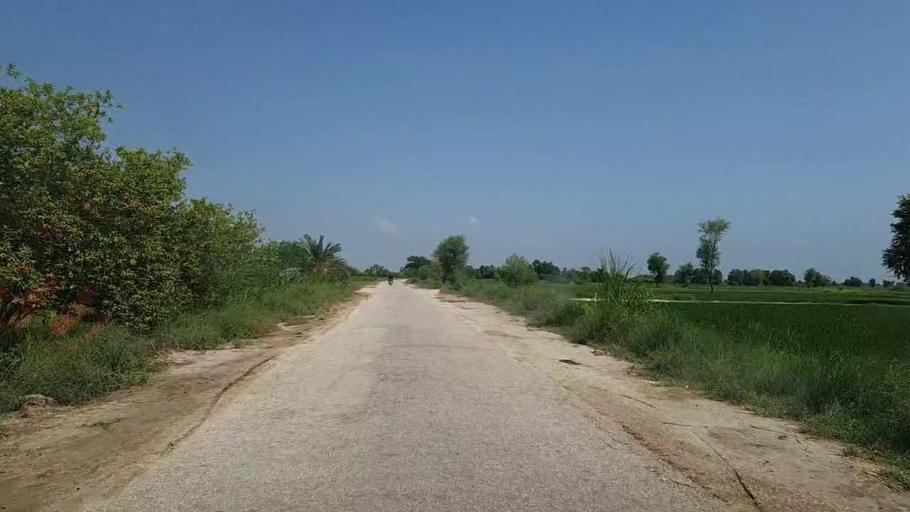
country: PK
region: Sindh
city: Bhiria
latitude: 26.8969
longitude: 68.2191
